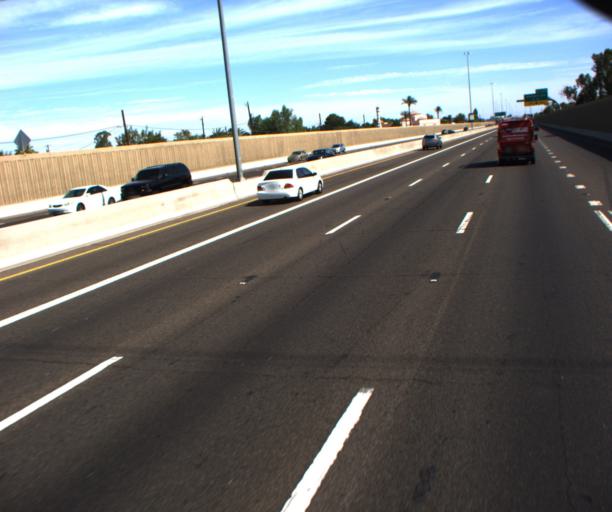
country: US
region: Arizona
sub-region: Maricopa County
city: Glendale
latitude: 33.5422
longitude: -112.1122
